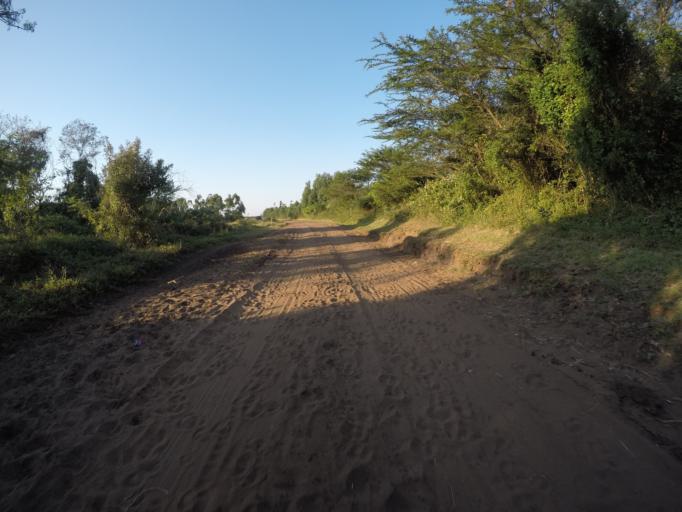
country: ZA
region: KwaZulu-Natal
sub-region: uThungulu District Municipality
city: KwaMbonambi
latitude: -28.6911
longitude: 32.2035
